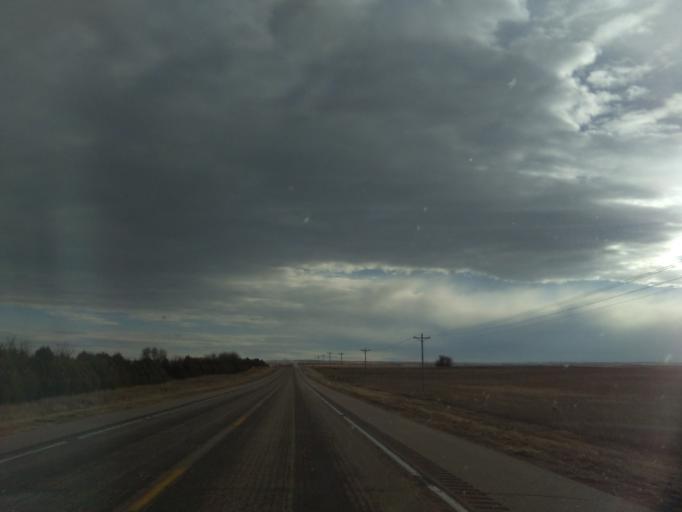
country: US
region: Nebraska
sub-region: Morrill County
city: Bridgeport
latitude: 41.5620
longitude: -102.9846
